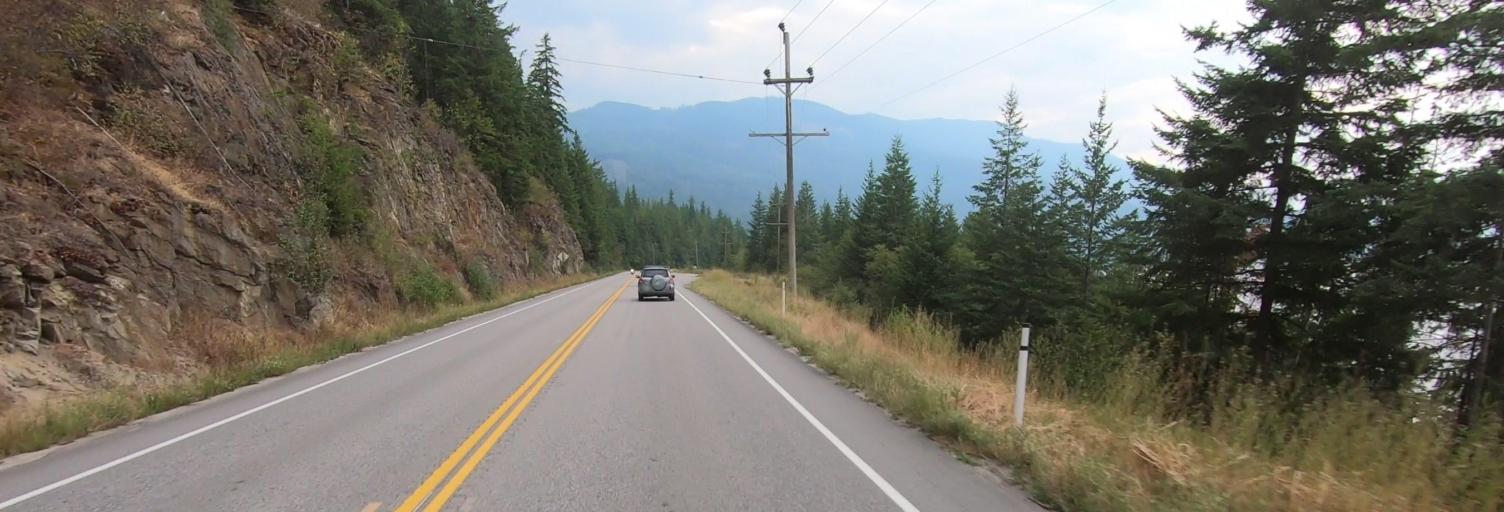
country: CA
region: British Columbia
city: Sicamous
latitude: 50.8048
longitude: -119.0622
